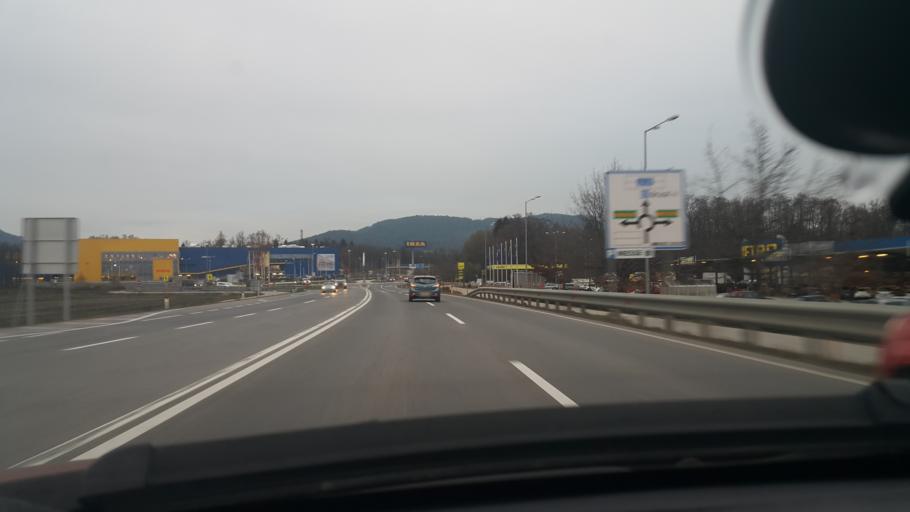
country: AT
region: Carinthia
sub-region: Politischer Bezirk Klagenfurt Land
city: Ebenthal
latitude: 46.6363
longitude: 14.3702
